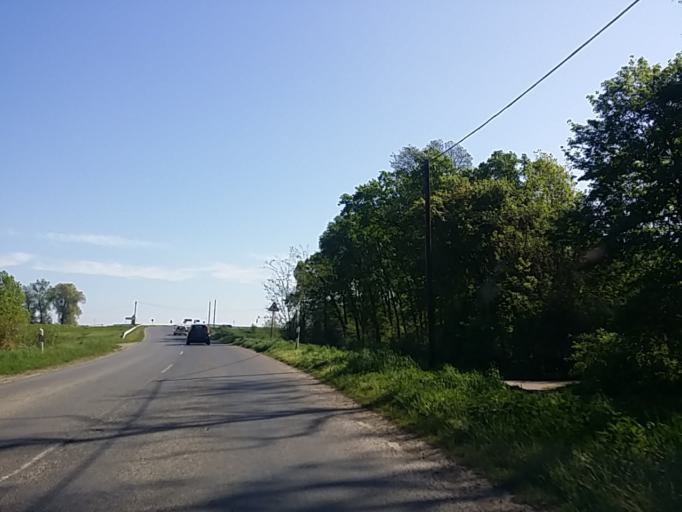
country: HU
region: Bekes
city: Doboz
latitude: 46.7236
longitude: 21.2166
